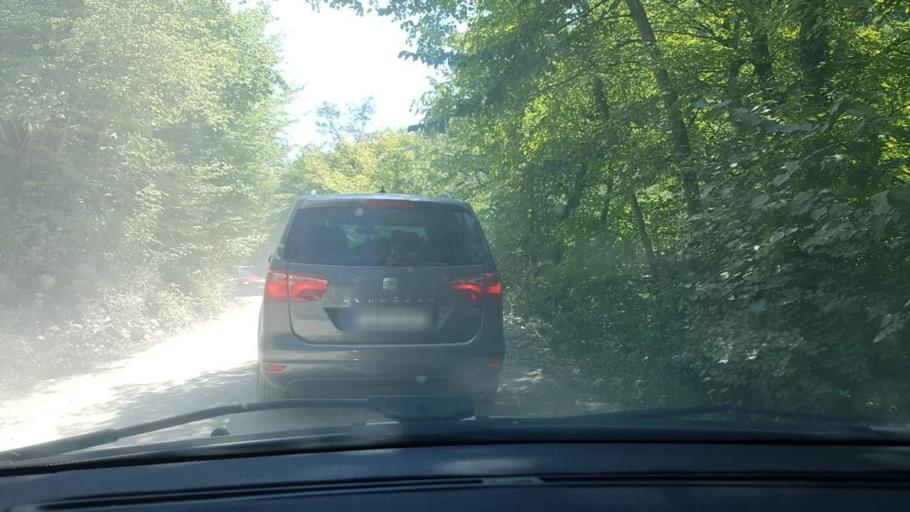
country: BA
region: Federation of Bosnia and Herzegovina
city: Orasac
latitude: 44.6485
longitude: 16.0324
